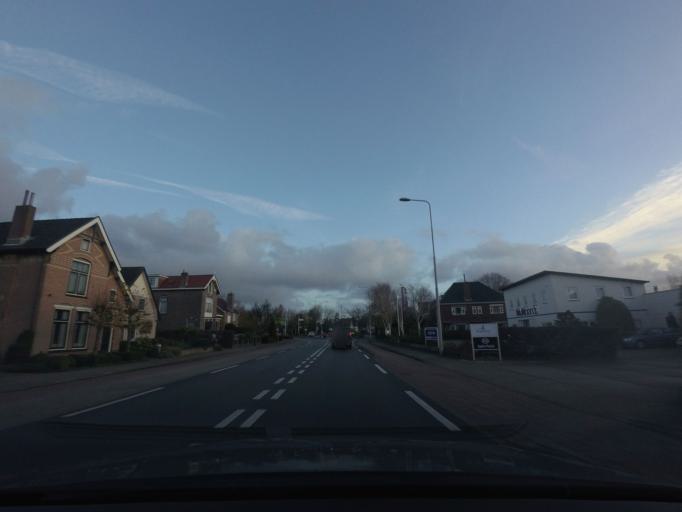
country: NL
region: South Holland
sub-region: Gemeente Lisse
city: Lisse
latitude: 52.2530
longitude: 4.5474
